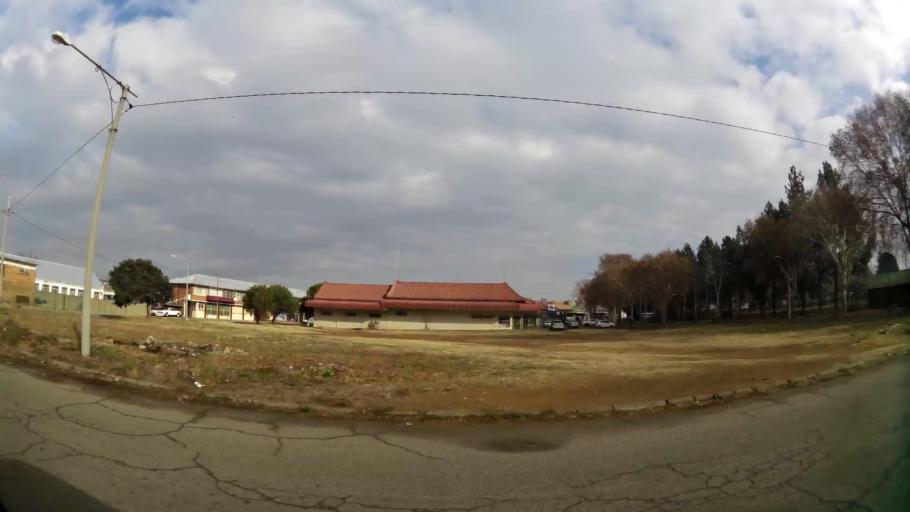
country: ZA
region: Gauteng
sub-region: Sedibeng District Municipality
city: Vanderbijlpark
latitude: -26.7031
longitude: 27.8182
